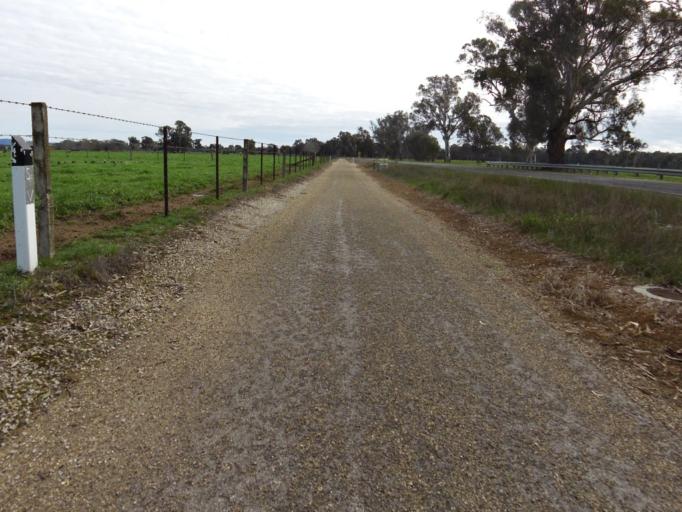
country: AU
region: Victoria
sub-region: Wangaratta
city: Wangaratta
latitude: -36.4148
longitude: 146.3541
